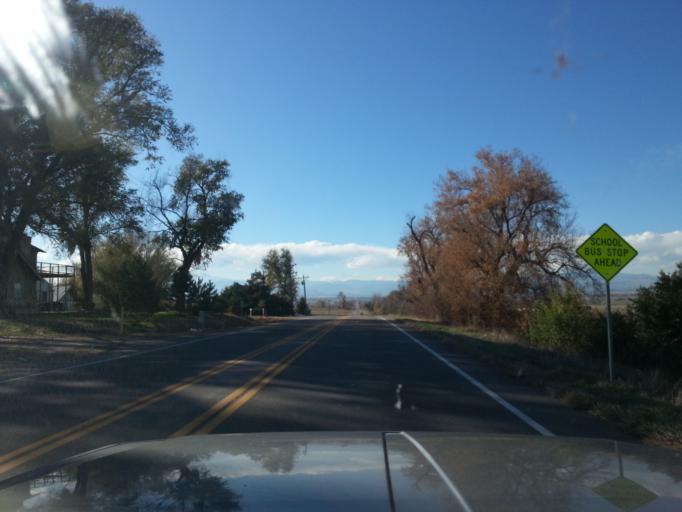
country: US
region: Colorado
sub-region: Larimer County
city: Loveland
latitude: 40.3782
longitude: -105.0159
